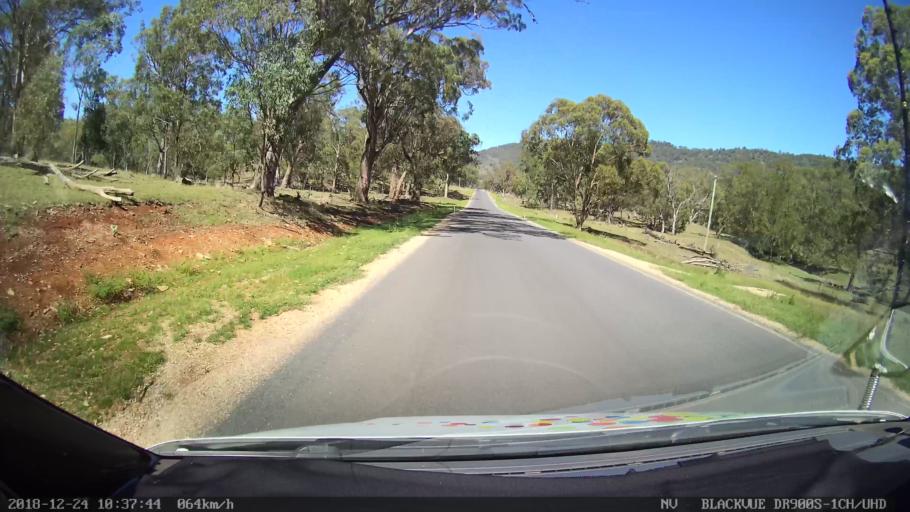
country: AU
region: New South Wales
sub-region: Upper Hunter Shire
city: Merriwa
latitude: -31.8467
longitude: 150.4904
